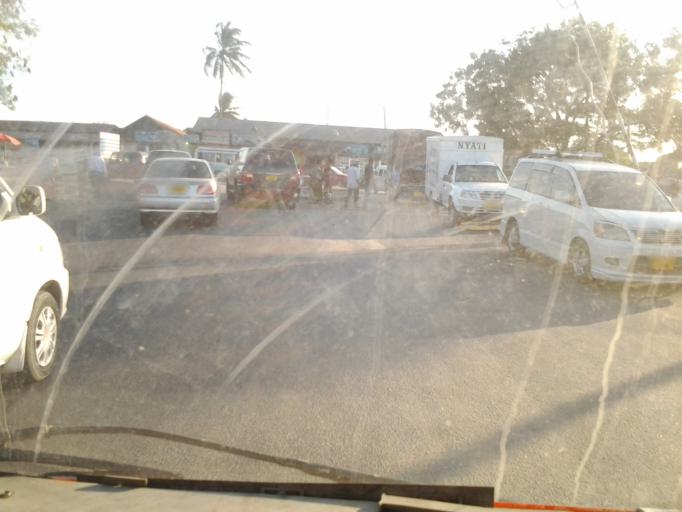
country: TZ
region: Dar es Salaam
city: Magomeni
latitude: -6.8250
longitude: 39.2312
